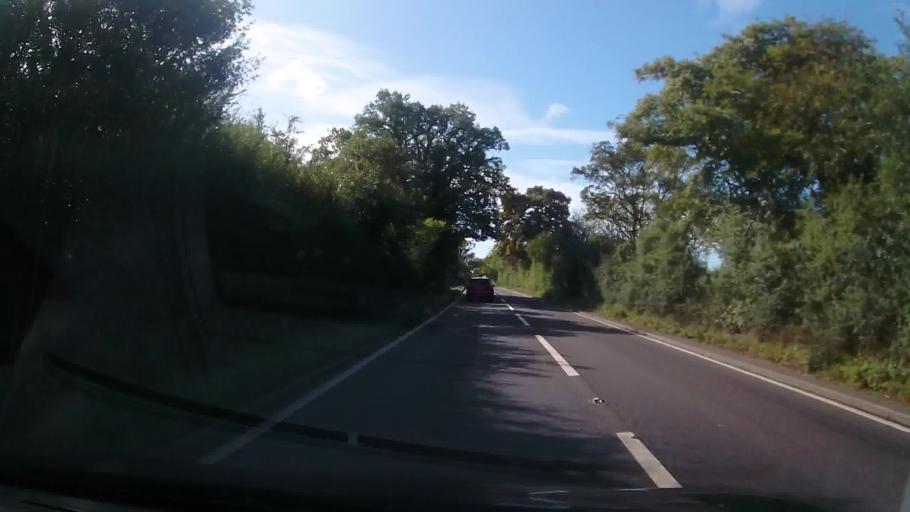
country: GB
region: England
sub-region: Shropshire
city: Astley
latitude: 52.7653
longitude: -2.7145
